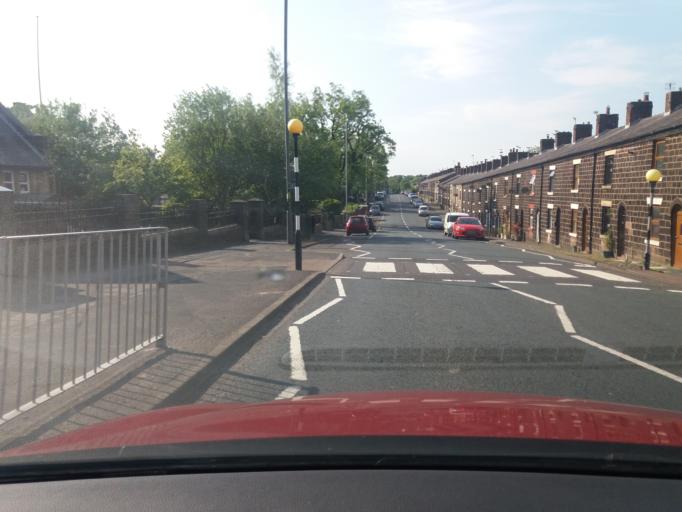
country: GB
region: England
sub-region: Blackburn with Darwen
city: Darwen
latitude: 53.6977
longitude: -2.5437
